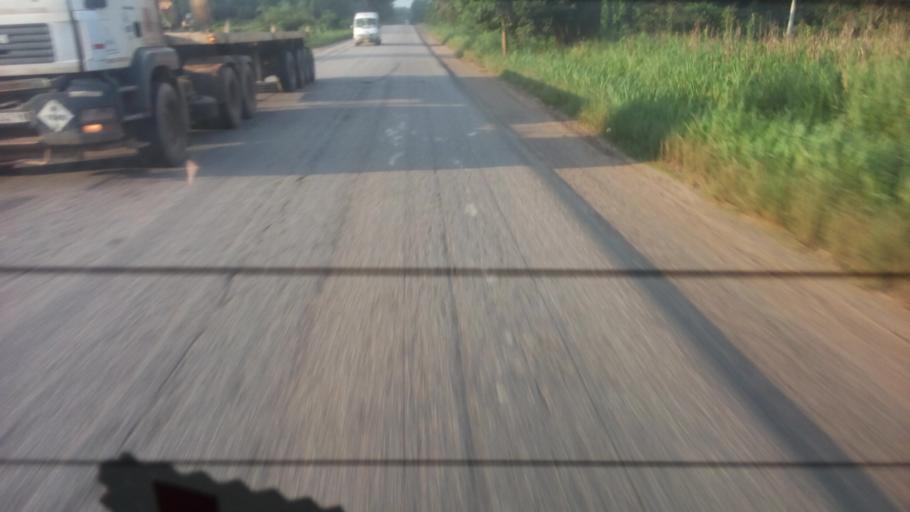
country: GH
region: Western
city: Tarkwa
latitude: 5.1960
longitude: -2.0319
